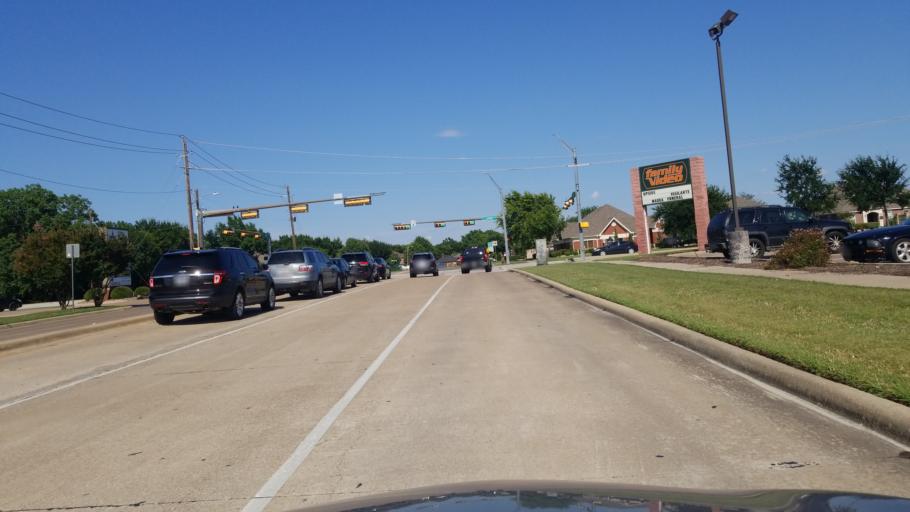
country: US
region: Texas
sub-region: Dallas County
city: Grand Prairie
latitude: 32.6920
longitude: -97.0164
